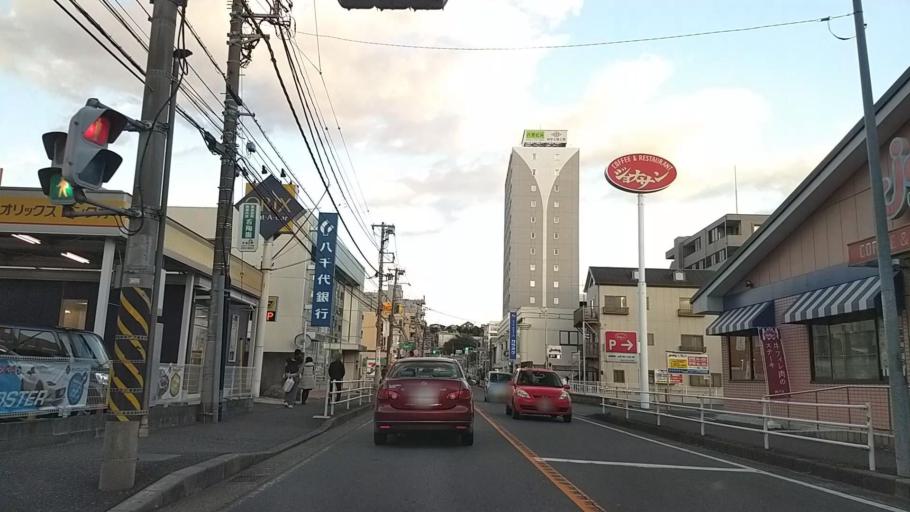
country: JP
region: Kanagawa
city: Atsugi
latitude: 35.4514
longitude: 139.3937
